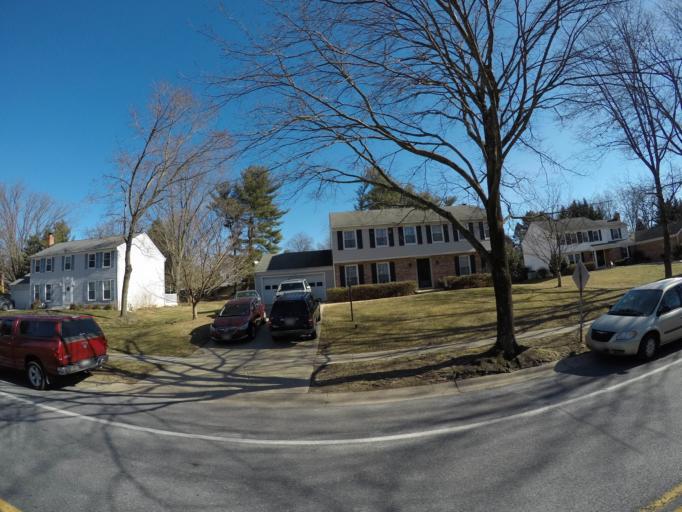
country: US
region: Maryland
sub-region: Howard County
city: Columbia
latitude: 39.2157
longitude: -76.8161
